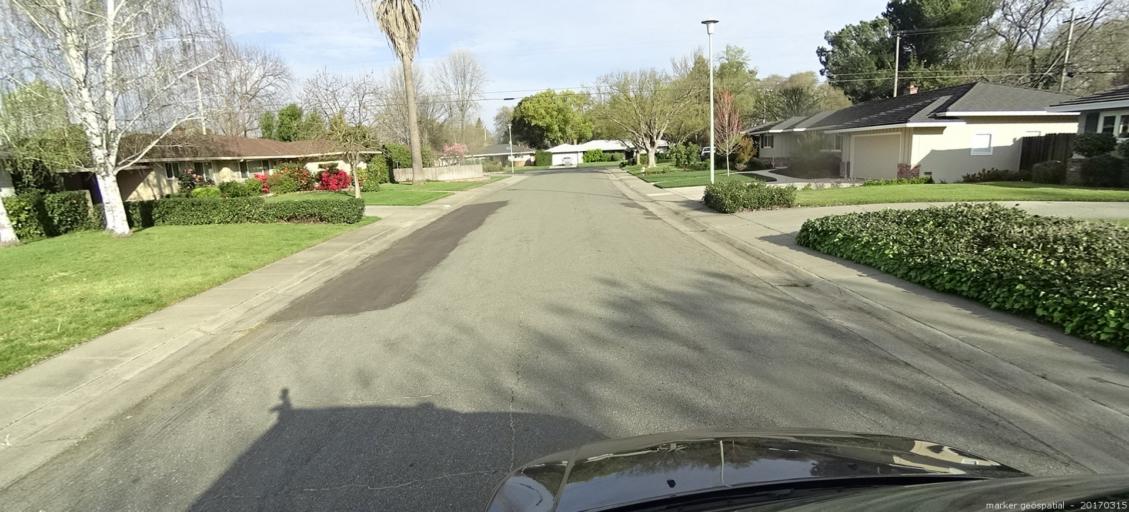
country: US
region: California
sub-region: Sacramento County
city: Parkway
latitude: 38.5053
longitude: -121.5121
